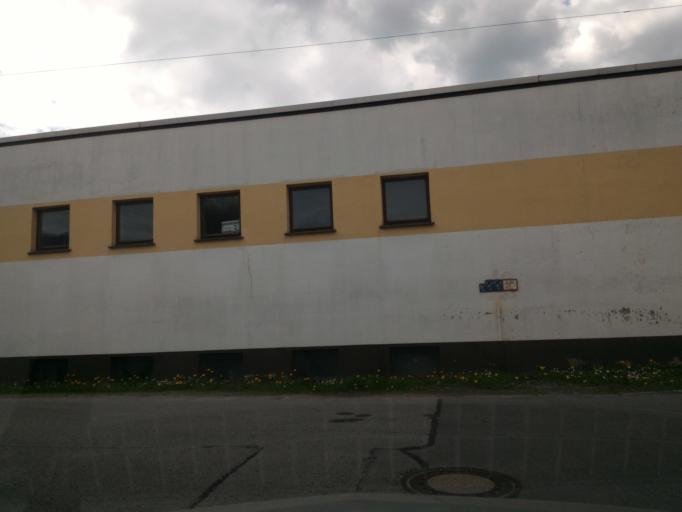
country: DE
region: Saxony
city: Neugersdorf
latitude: 50.9846
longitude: 14.6120
